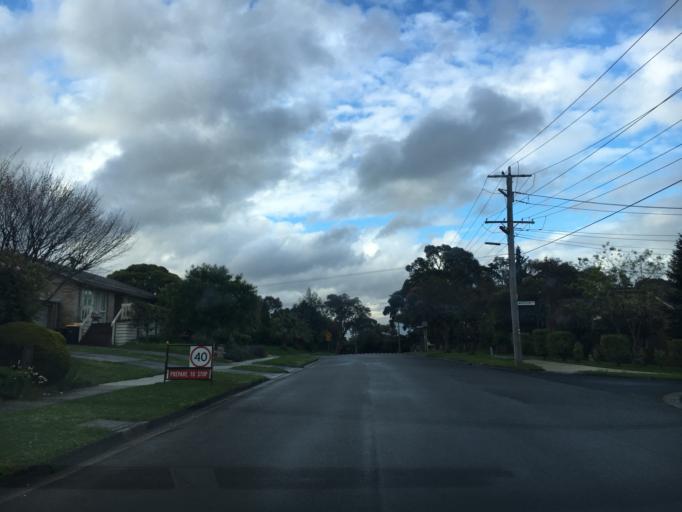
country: AU
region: Victoria
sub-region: Whitehorse
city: Vermont South
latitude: -37.8821
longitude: 145.1820
